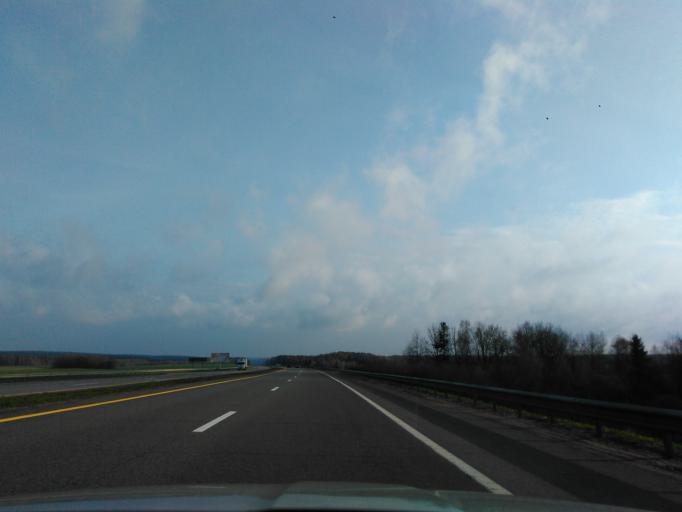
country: BY
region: Minsk
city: Lahoysk
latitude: 54.1540
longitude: 27.8107
